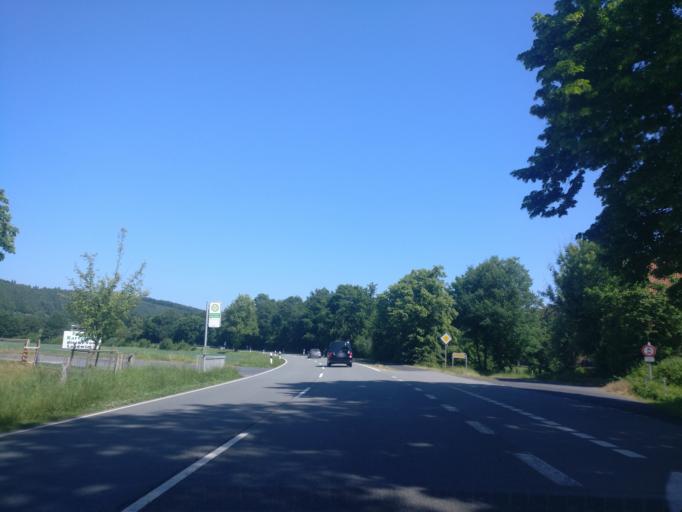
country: DE
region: Lower Saxony
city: Hannoversch Munden
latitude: 51.4467
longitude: 9.6388
